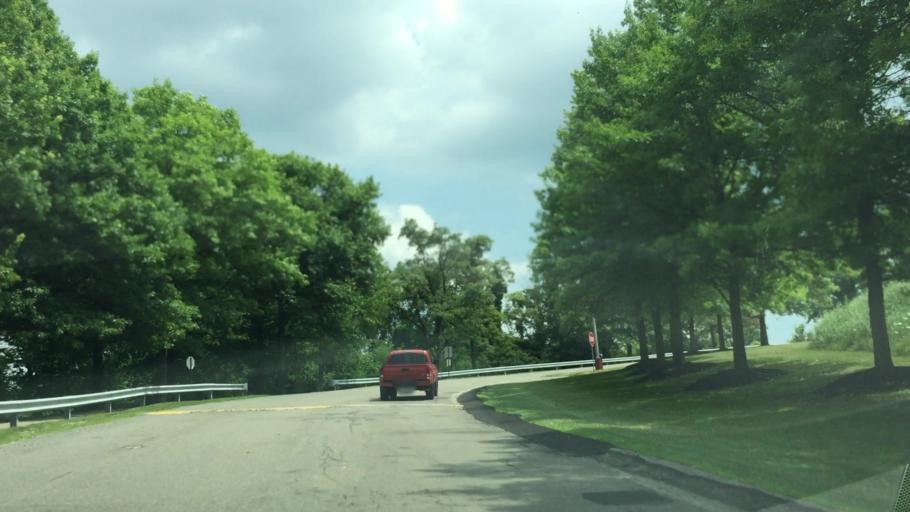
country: US
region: Pennsylvania
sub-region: Allegheny County
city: Imperial
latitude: 40.4460
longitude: -80.2377
